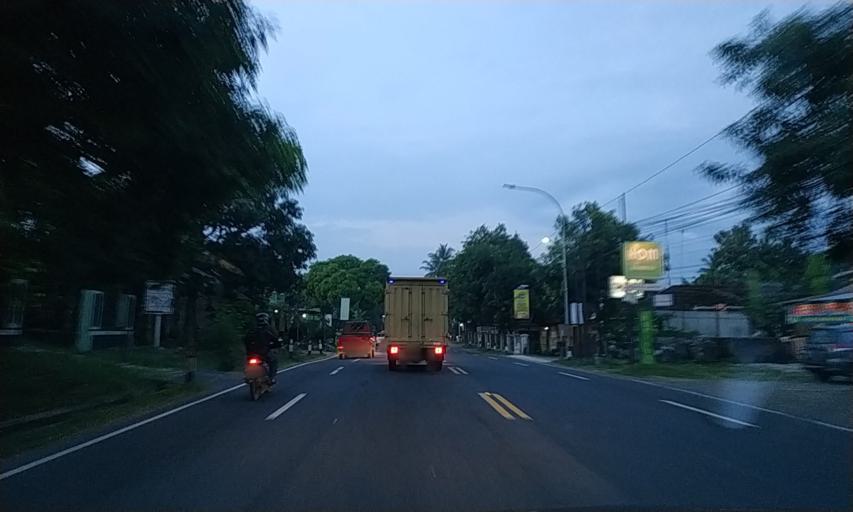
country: ID
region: Daerah Istimewa Yogyakarta
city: Godean
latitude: -7.8309
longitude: 110.2212
